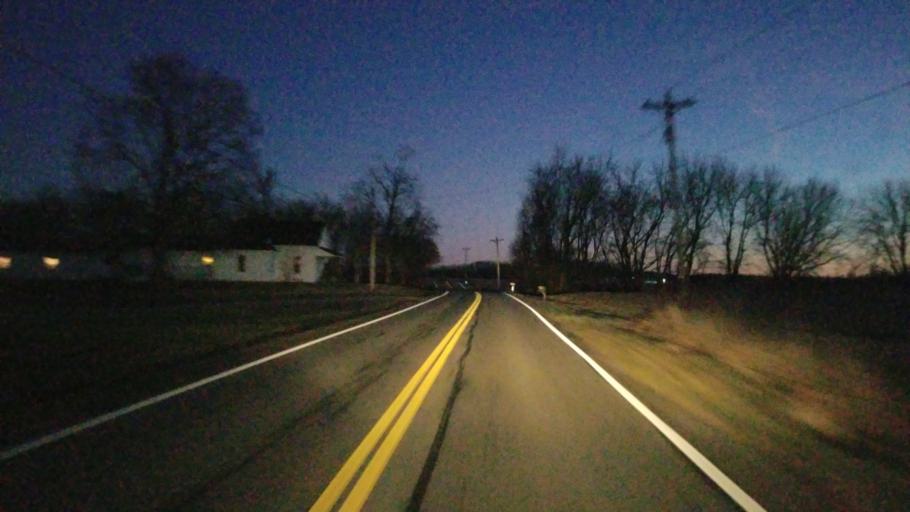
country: US
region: Ohio
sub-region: Highland County
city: Leesburg
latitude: 39.3192
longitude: -83.5347
